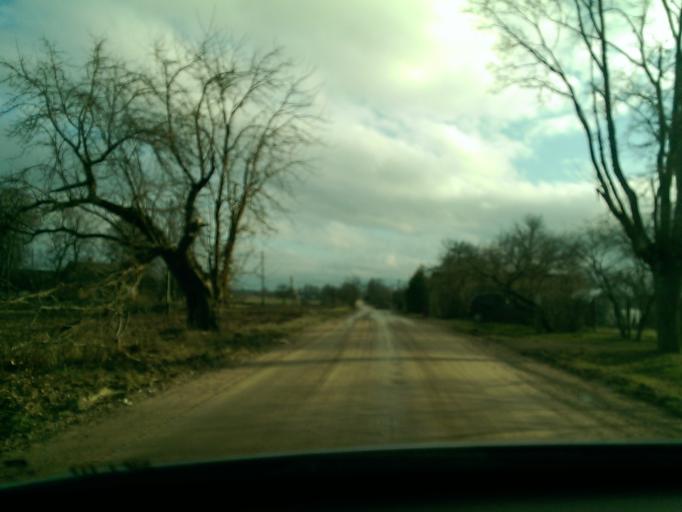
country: LV
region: Kuldigas Rajons
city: Kuldiga
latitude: 56.9790
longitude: 21.9841
